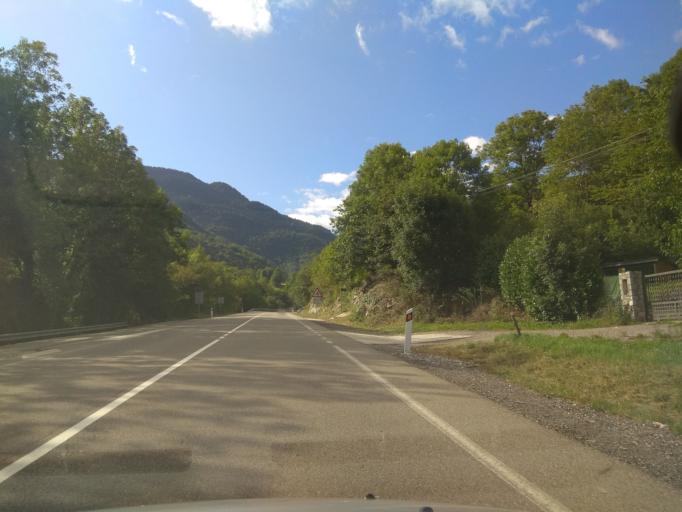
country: ES
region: Catalonia
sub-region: Provincia de Lleida
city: Les
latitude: 42.7933
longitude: 0.6980
